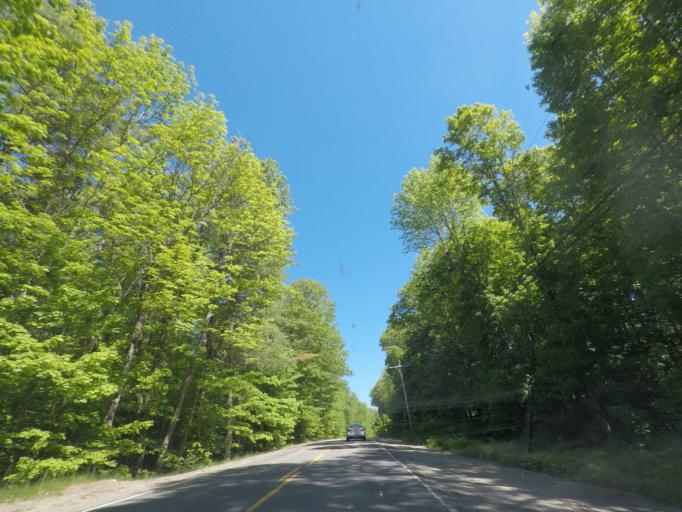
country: US
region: Maine
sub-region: Kennebec County
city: Manchester
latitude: 44.2912
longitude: -69.8890
